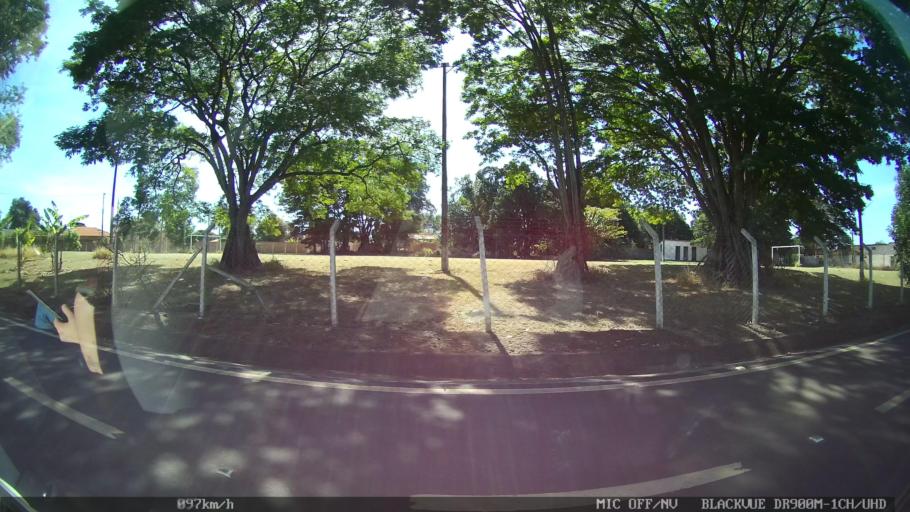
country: BR
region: Sao Paulo
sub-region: Franca
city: Franca
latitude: -20.5558
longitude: -47.5707
